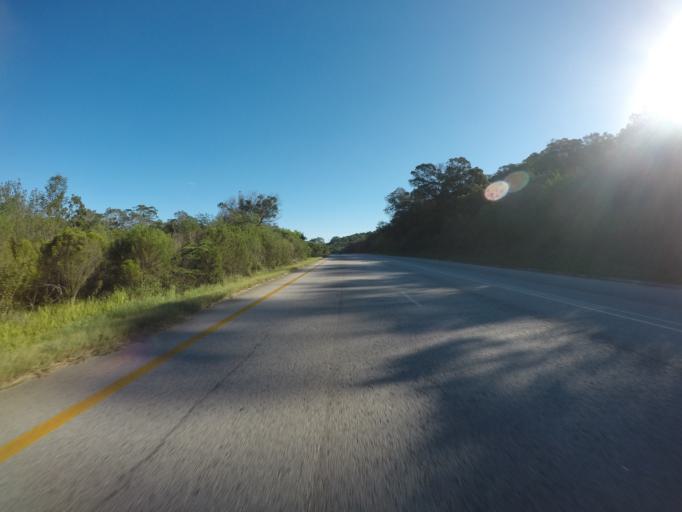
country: ZA
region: Eastern Cape
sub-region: Cacadu District Municipality
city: Jeffrey's Bay
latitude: -33.9030
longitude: 25.0824
